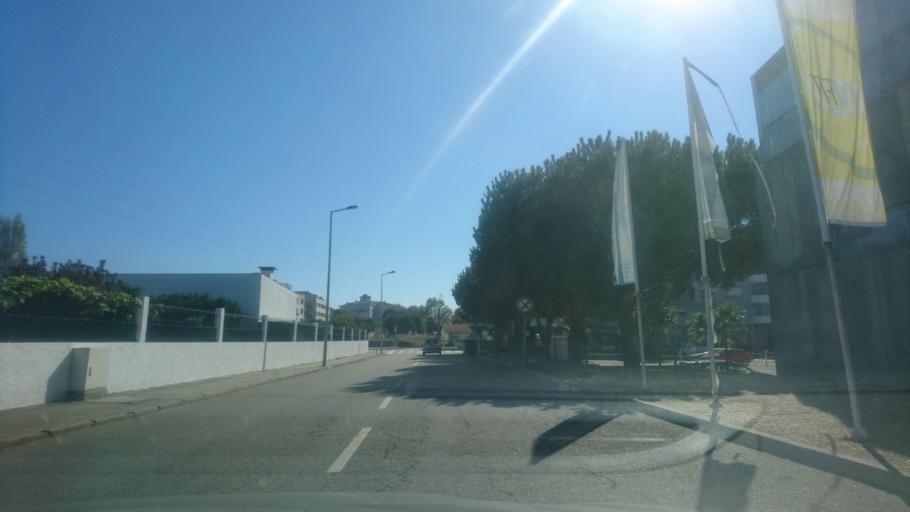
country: PT
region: Aveiro
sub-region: Ovar
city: Esmoriz
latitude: 40.9586
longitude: -8.6321
